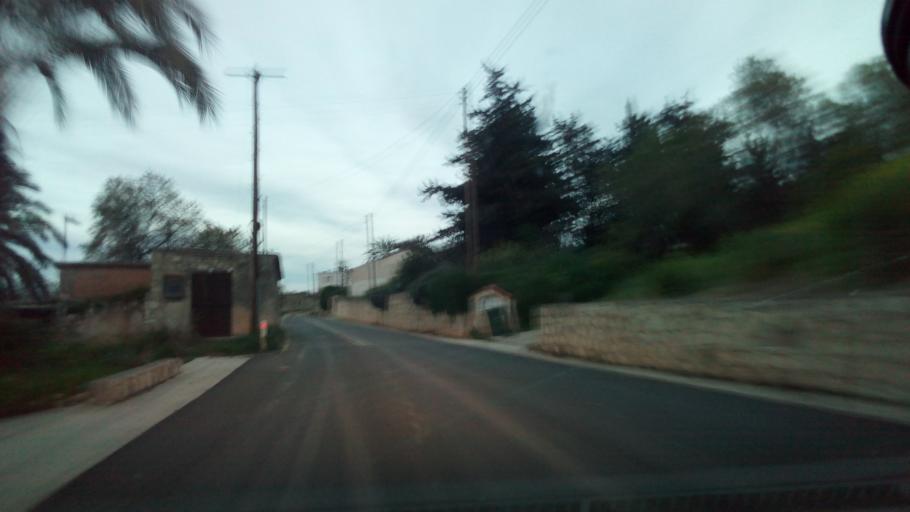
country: CY
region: Pafos
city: Polis
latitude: 34.9876
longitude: 32.5053
